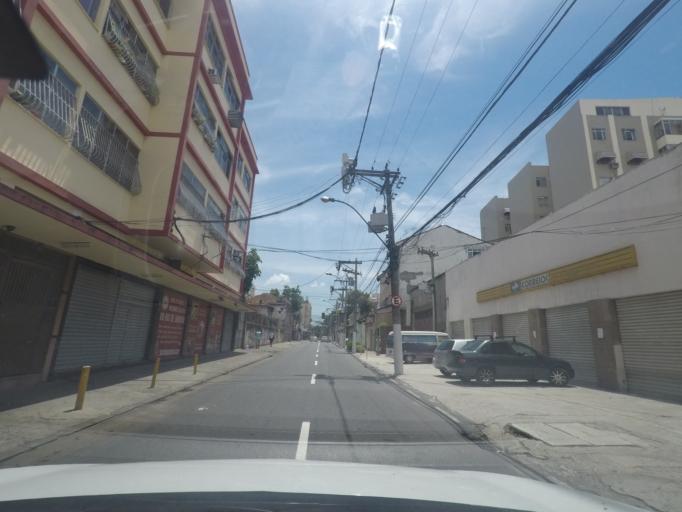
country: BR
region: Rio de Janeiro
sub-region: Niteroi
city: Niteroi
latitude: -22.8874
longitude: -43.1237
